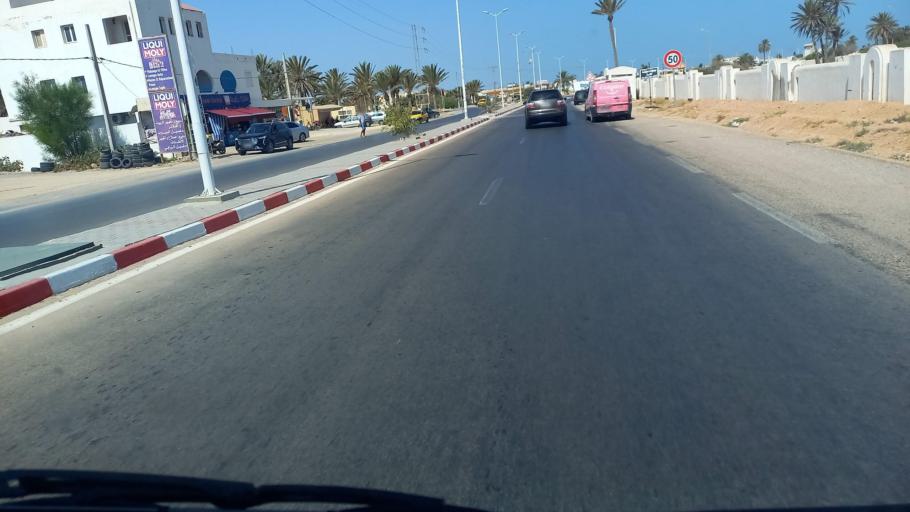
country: TN
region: Madanin
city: Midoun
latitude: 33.8615
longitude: 10.9668
